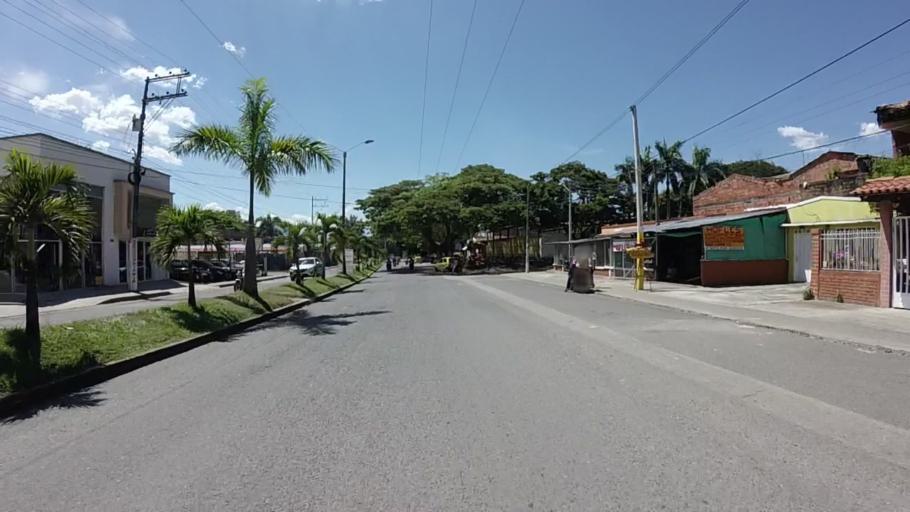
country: CO
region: Valle del Cauca
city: Cartago
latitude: 4.7382
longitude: -75.9092
